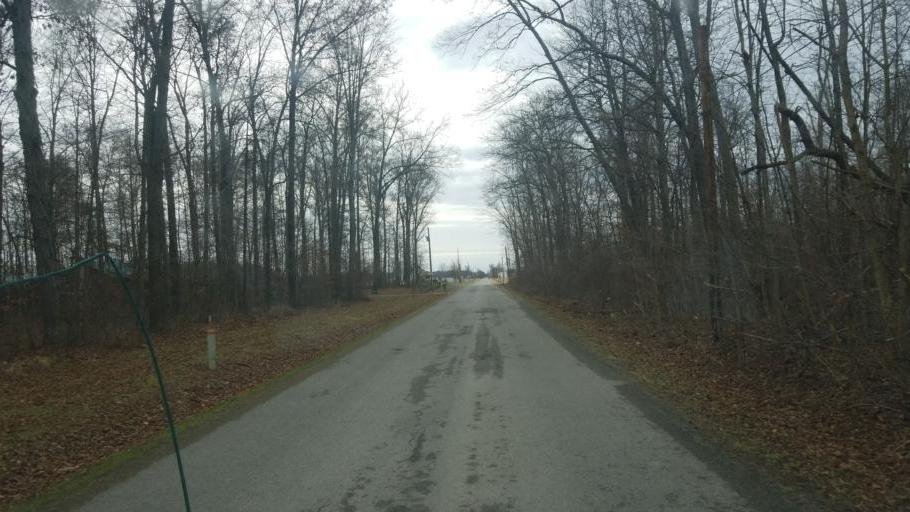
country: US
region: Ohio
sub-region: Morrow County
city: Cardington
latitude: 40.4489
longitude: -82.8963
